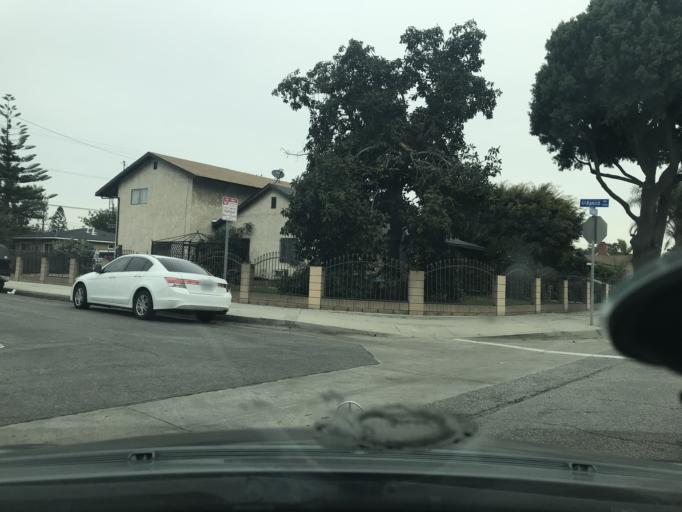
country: US
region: California
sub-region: Los Angeles County
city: Bell Gardens
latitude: 33.9598
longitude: -118.1502
